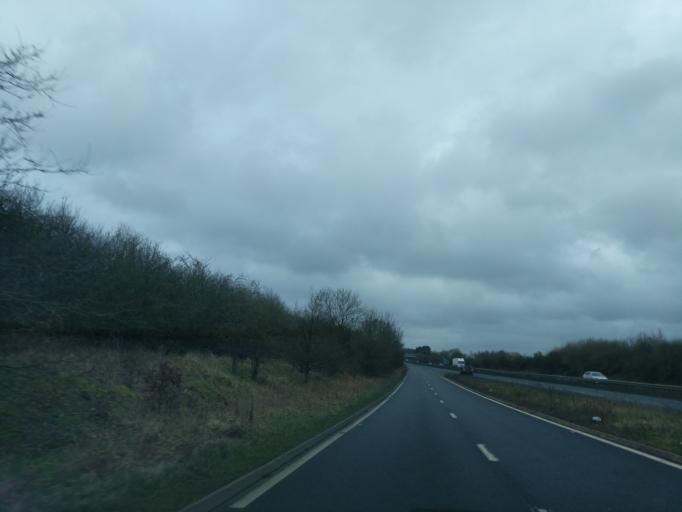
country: GB
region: England
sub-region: Staffordshire
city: Lichfield
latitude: 52.6607
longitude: -1.8163
